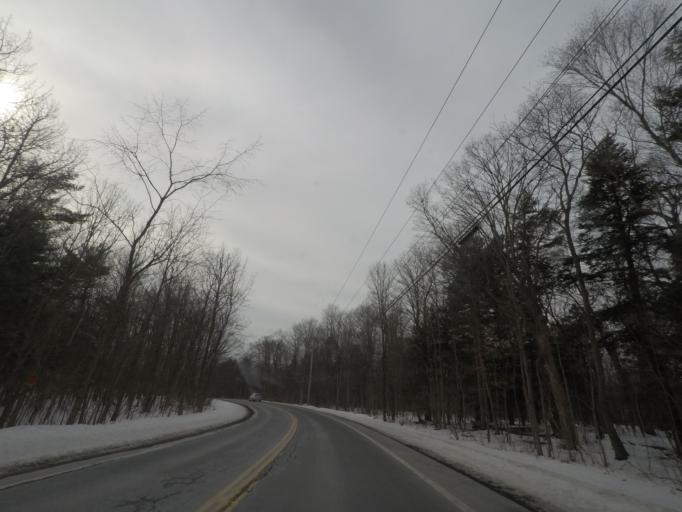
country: US
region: New York
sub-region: Albany County
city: Altamont
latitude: 42.6809
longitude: -74.0917
